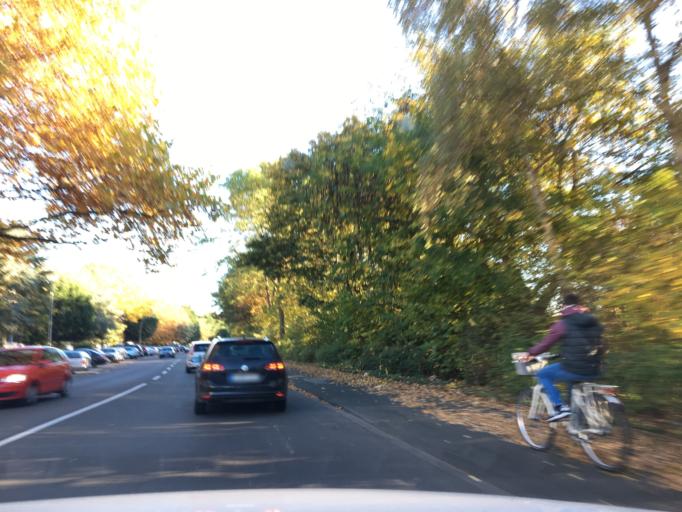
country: DE
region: North Rhine-Westphalia
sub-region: Regierungsbezirk Koln
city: Bilderstoeckchen
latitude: 50.9720
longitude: 6.9238
